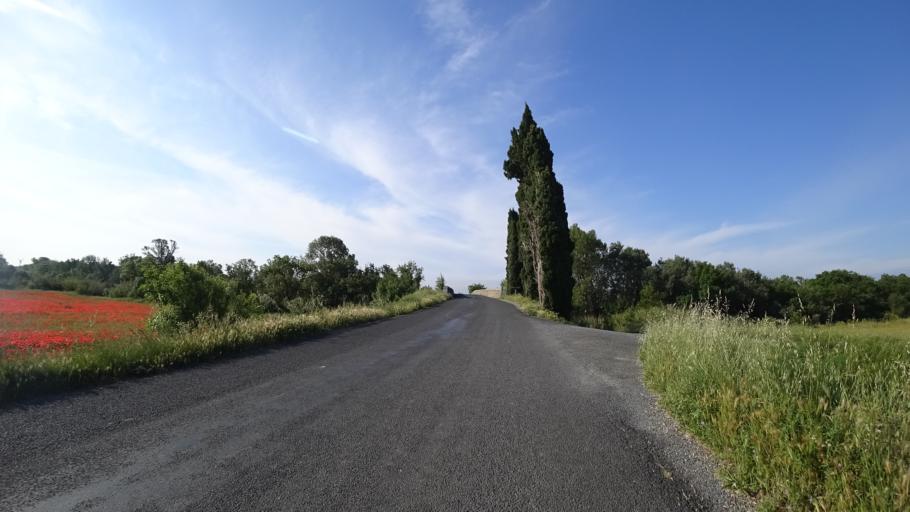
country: FR
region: Languedoc-Roussillon
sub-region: Departement de l'Aude
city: Canet
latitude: 43.2393
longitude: 2.7982
